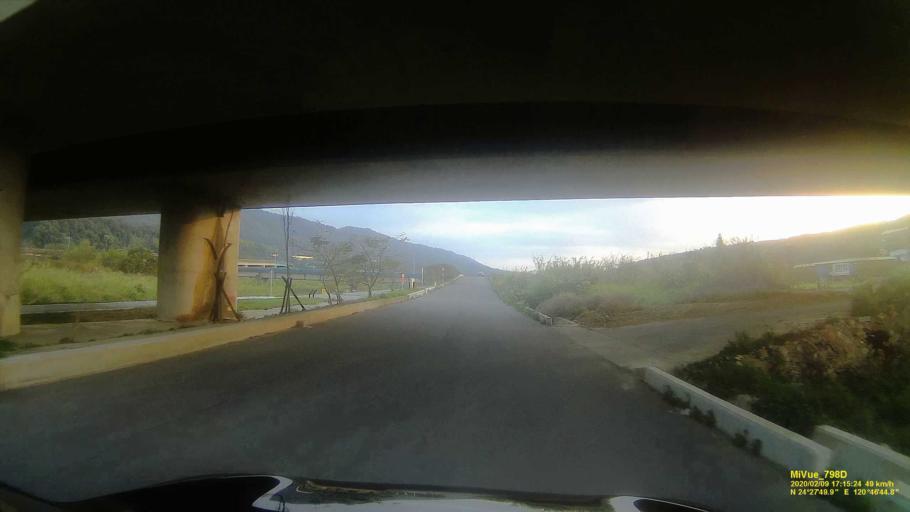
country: TW
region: Taiwan
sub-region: Miaoli
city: Miaoli
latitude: 24.4637
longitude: 120.7791
